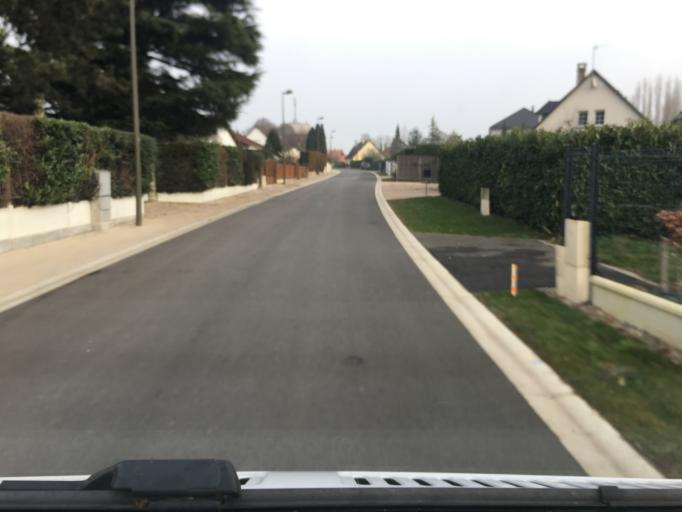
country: FR
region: Picardie
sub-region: Departement de la Somme
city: Saint-Valery-sur-Somme
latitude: 50.1781
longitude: 1.6303
